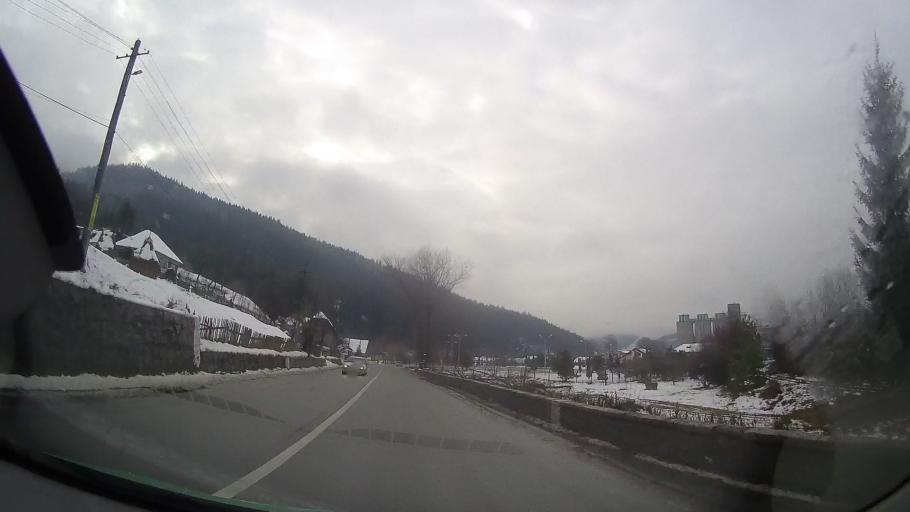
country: RO
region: Neamt
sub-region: Comuna Tasca
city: Tasca
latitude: 46.8967
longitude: 26.0409
